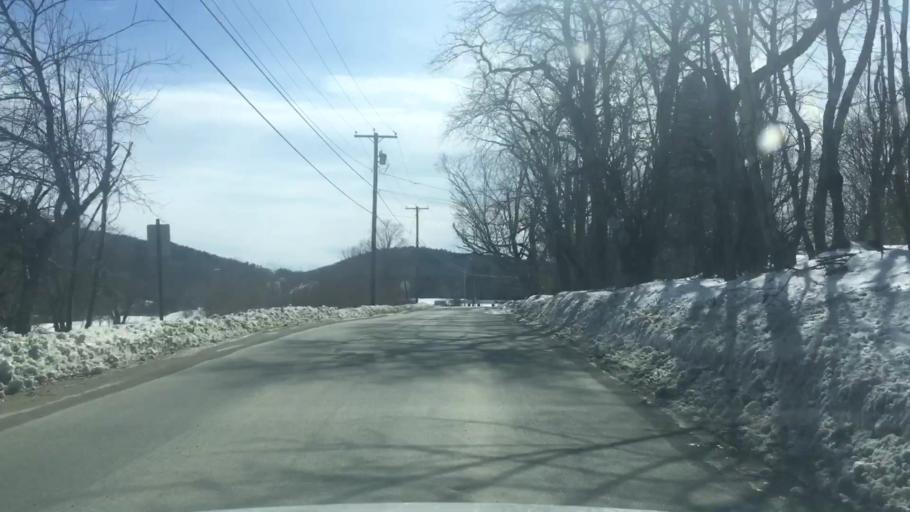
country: US
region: Maine
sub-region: Penobscot County
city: Holden
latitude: 44.7390
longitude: -68.6287
